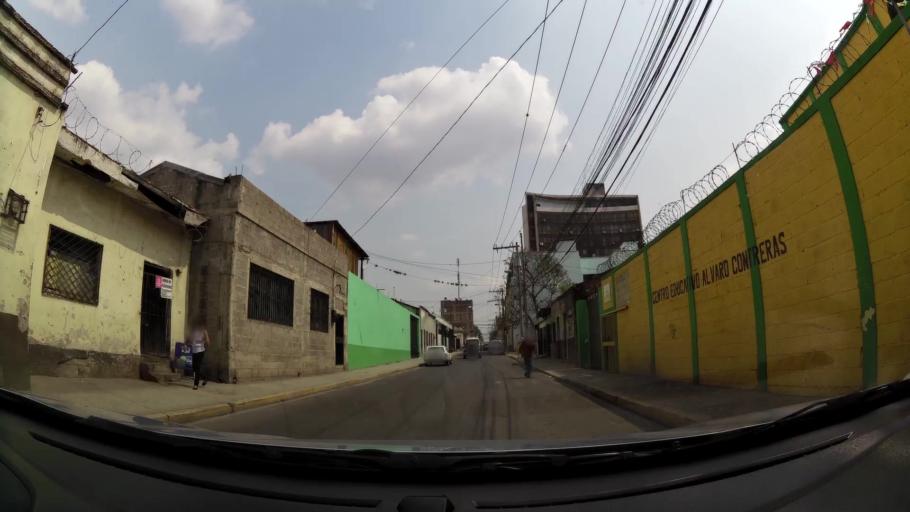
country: HN
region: Francisco Morazan
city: Tegucigalpa
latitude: 14.1099
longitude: -87.2089
